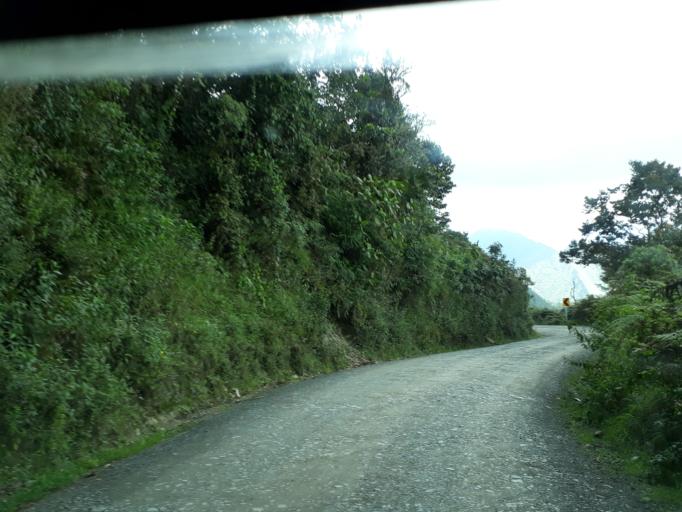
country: CO
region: Cundinamarca
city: Pacho
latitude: 5.2381
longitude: -74.1875
